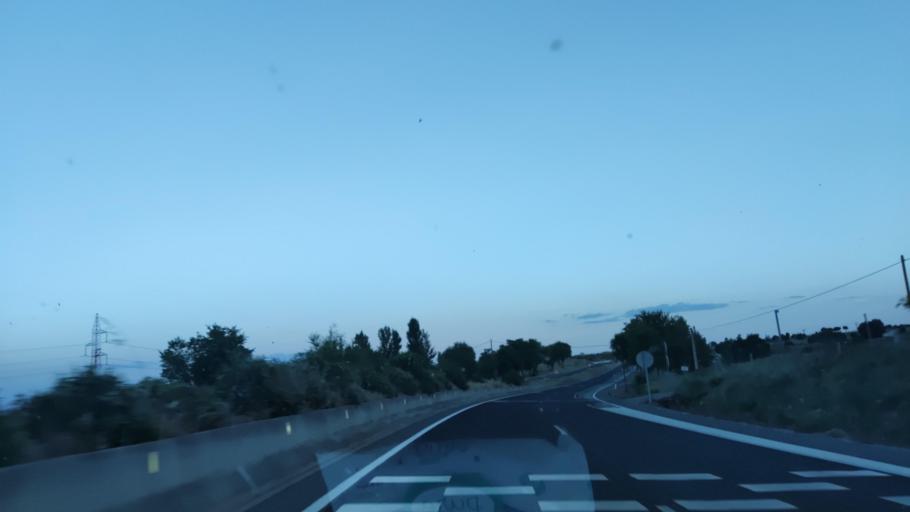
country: ES
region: Madrid
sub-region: Provincia de Madrid
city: San Sebastian de los Reyes
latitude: 40.5169
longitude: -3.5919
